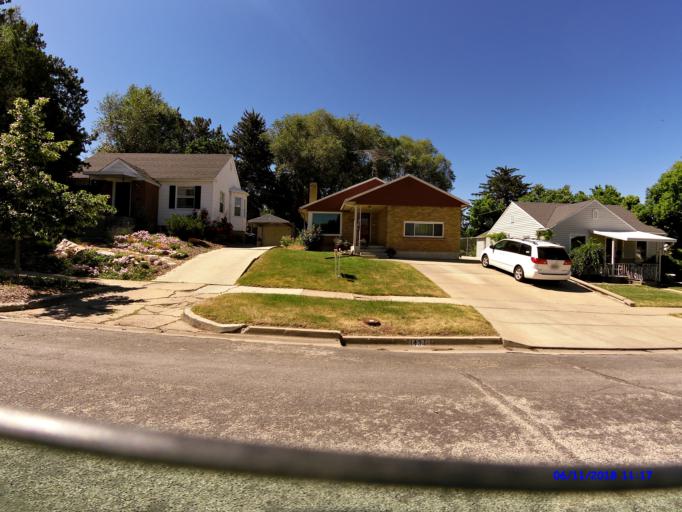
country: US
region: Utah
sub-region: Weber County
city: Ogden
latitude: 41.2213
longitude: -111.9416
